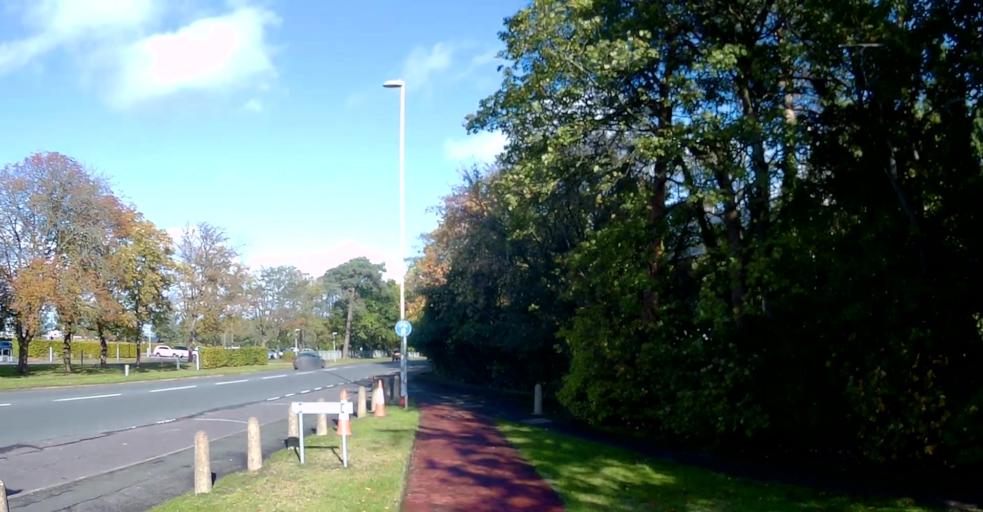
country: GB
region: England
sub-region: Hampshire
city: Farnborough
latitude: 51.2794
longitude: -0.7540
